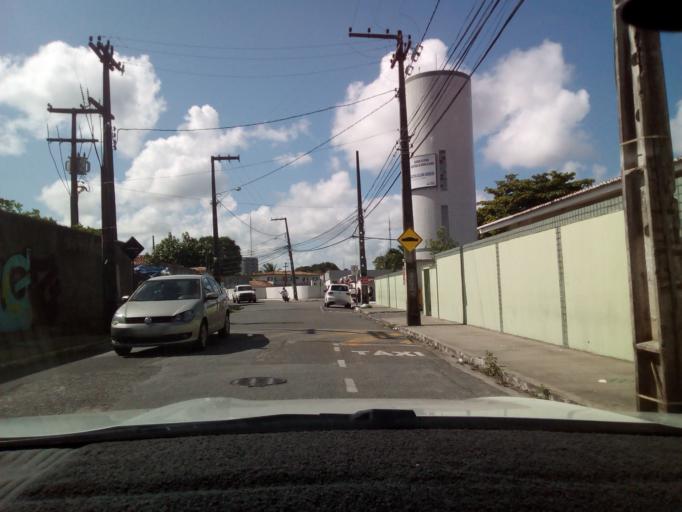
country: BR
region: Paraiba
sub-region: Joao Pessoa
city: Joao Pessoa
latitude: -7.1298
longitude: -34.8756
